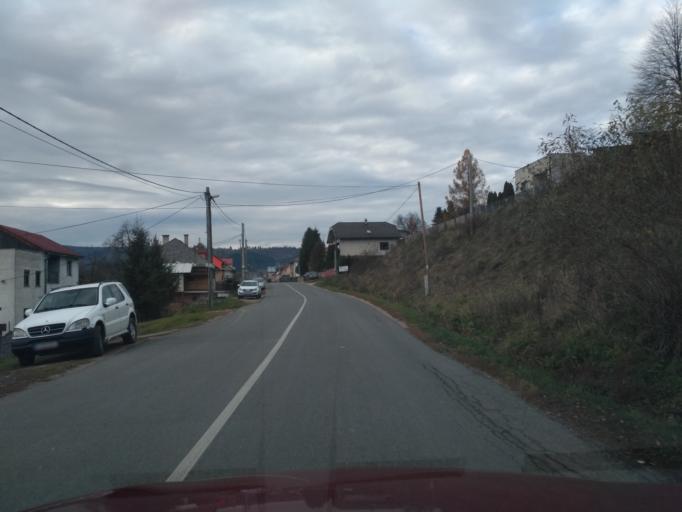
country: SK
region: Kosicky
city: Krompachy
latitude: 48.8111
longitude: 20.7203
